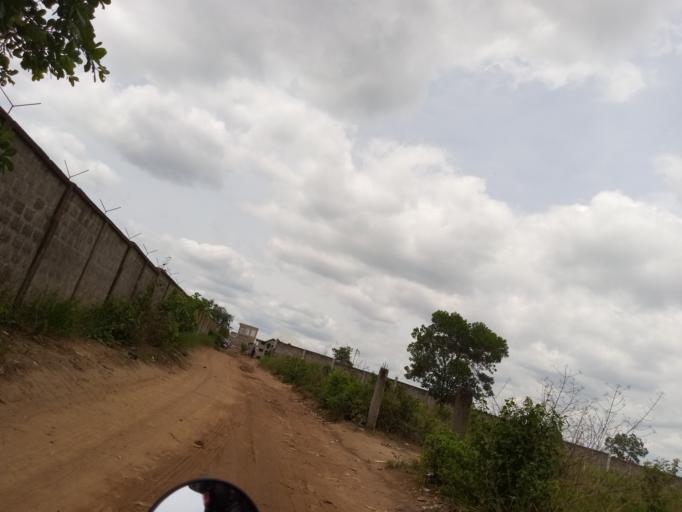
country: SL
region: Western Area
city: Waterloo
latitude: 8.3314
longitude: -13.0313
